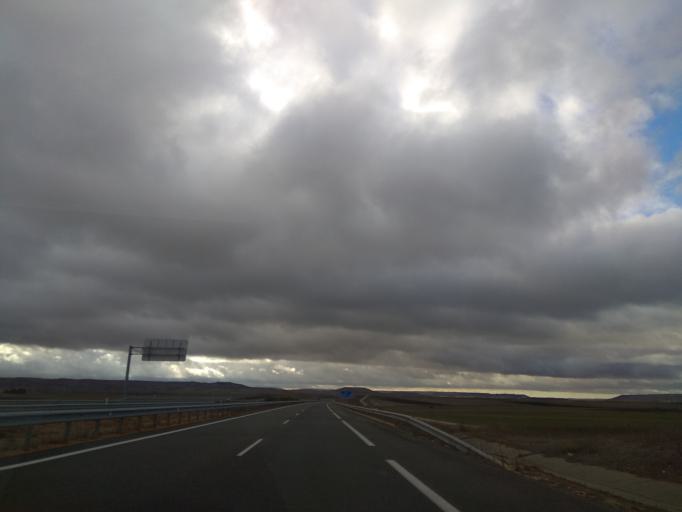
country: ES
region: Castille and Leon
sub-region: Provincia de Burgos
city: Quintanaortuno
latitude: 42.4476
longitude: -3.6911
